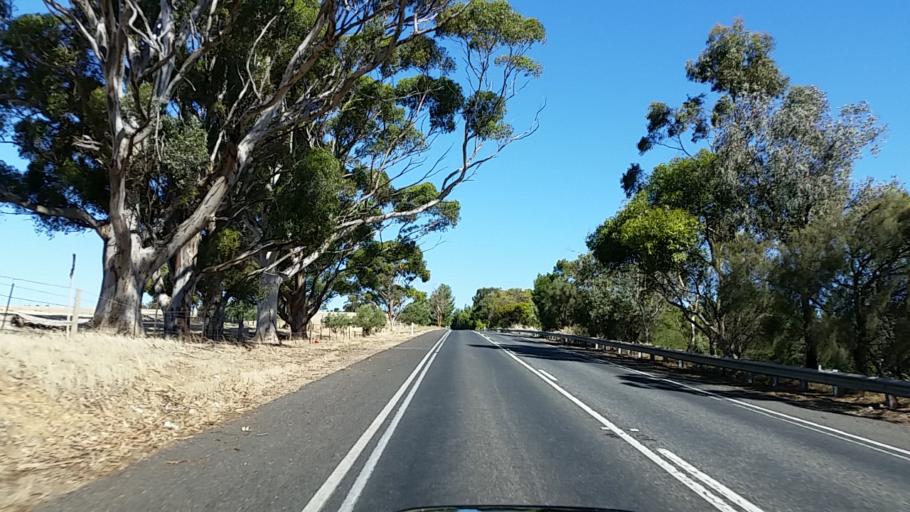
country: AU
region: South Australia
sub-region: Playford
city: One Tree Hill
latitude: -34.7137
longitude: 138.7364
